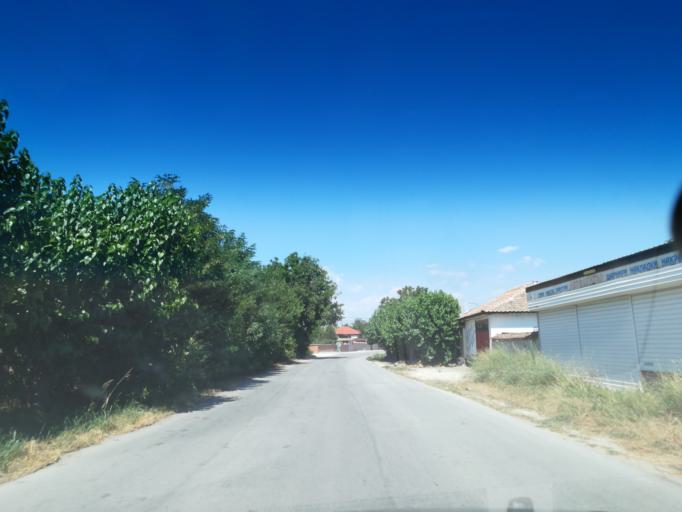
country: BG
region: Stara Zagora
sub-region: Obshtina Chirpan
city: Chirpan
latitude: 42.0742
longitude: 25.1872
